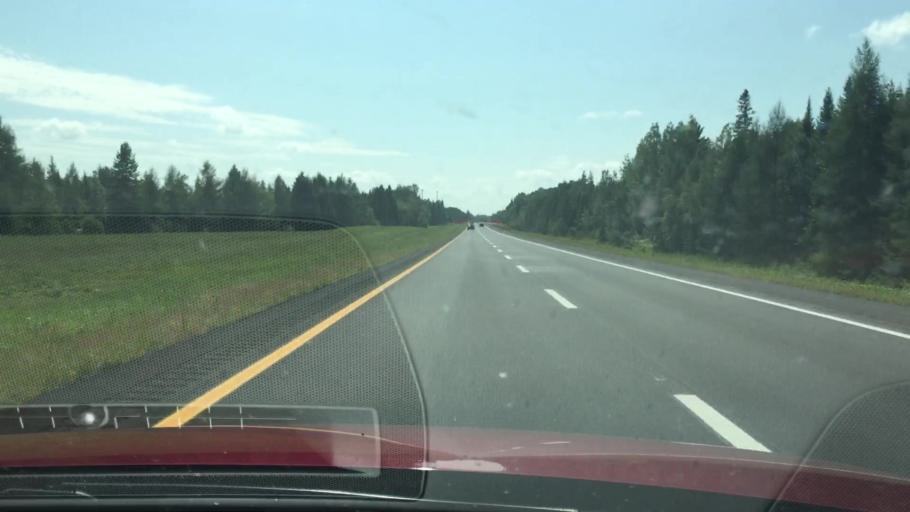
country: US
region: Maine
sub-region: Penobscot County
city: Patten
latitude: 45.8828
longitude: -68.4088
